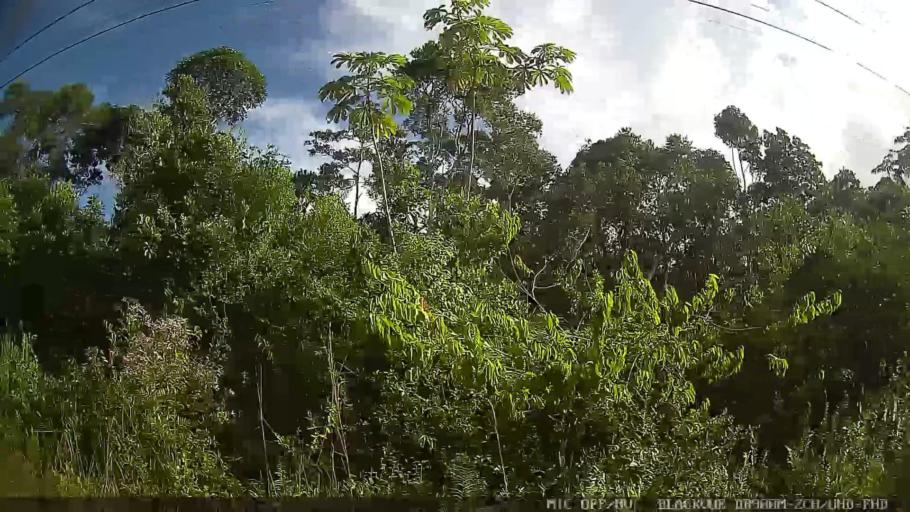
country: BR
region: Sao Paulo
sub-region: Itanhaem
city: Itanhaem
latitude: -24.2018
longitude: -46.8895
